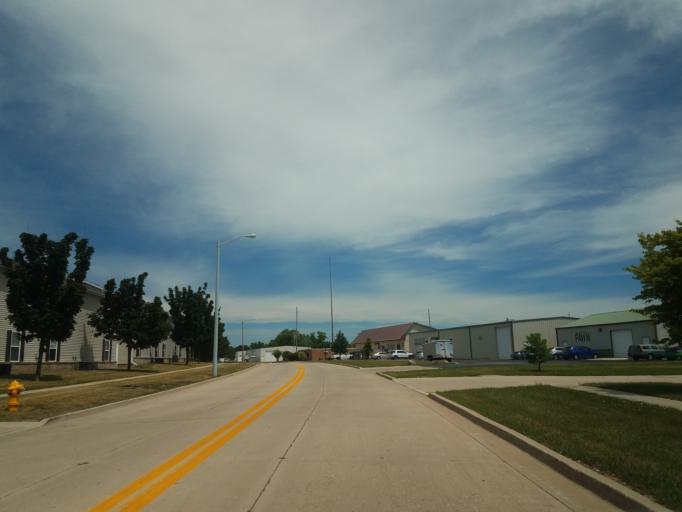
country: US
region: Illinois
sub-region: McLean County
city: Bloomington
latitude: 40.4616
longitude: -88.9884
